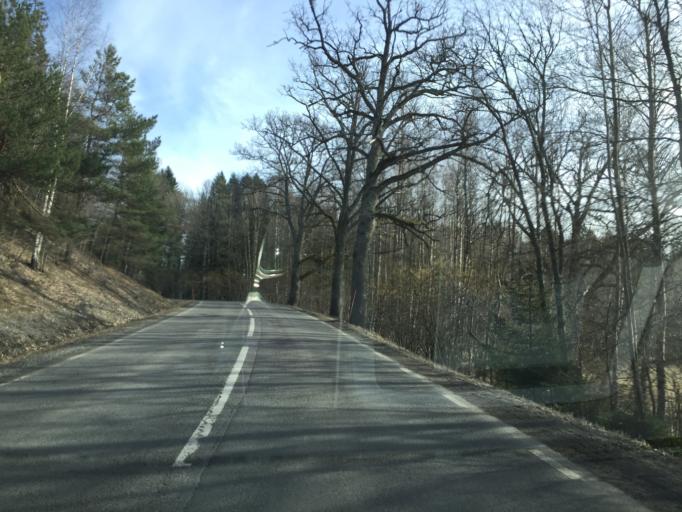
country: SE
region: Stockholm
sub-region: Huddinge Kommun
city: Huddinge
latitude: 59.1295
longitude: 17.9905
